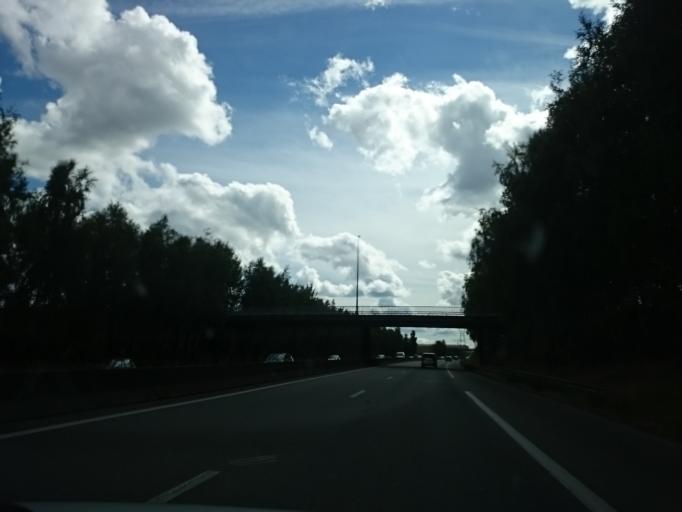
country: FR
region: Pays de la Loire
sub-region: Departement de la Loire-Atlantique
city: Saint-Sebastien-sur-Loire
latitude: 47.1962
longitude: -1.4860
